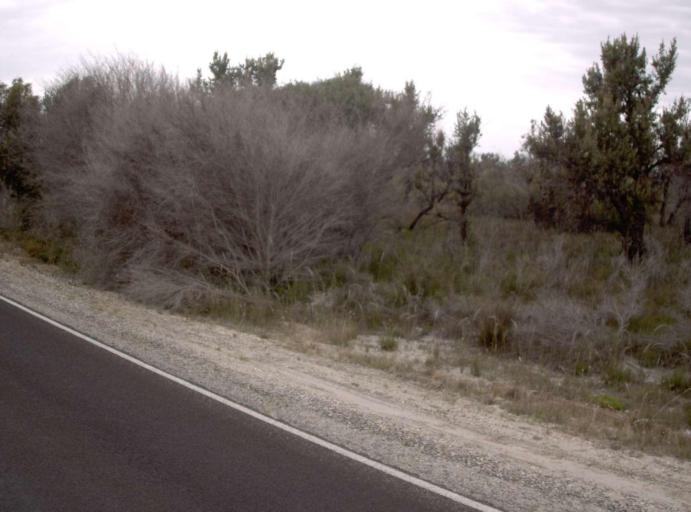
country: AU
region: Victoria
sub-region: East Gippsland
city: Bairnsdale
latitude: -38.1049
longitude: 147.4853
